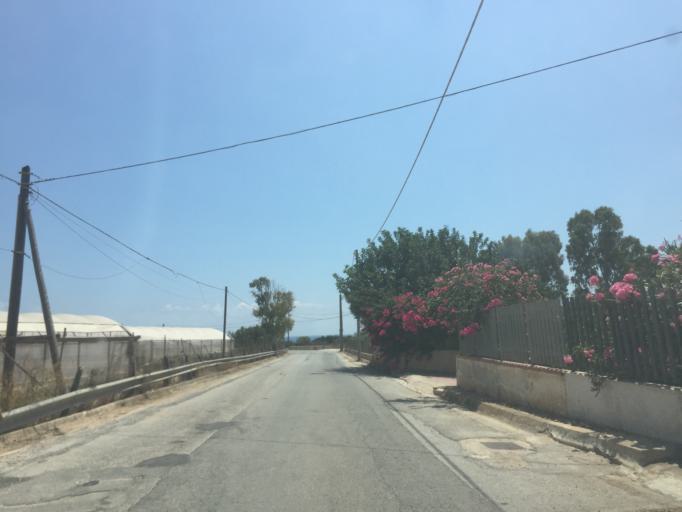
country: IT
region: Sicily
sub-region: Ragusa
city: Santa Croce Camerina
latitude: 36.8001
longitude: 14.5196
